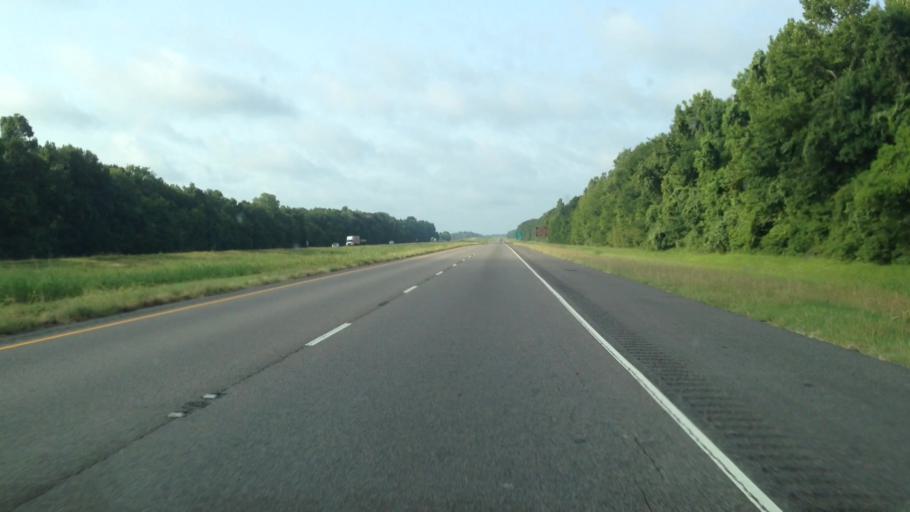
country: US
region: Louisiana
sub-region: Avoyelles Parish
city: Bunkie
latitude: 30.8852
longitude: -92.2275
